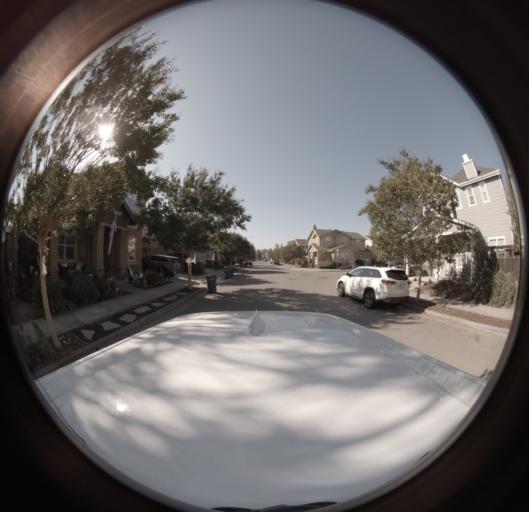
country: US
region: California
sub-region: Sonoma County
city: Petaluma
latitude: 38.2367
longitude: -122.5893
